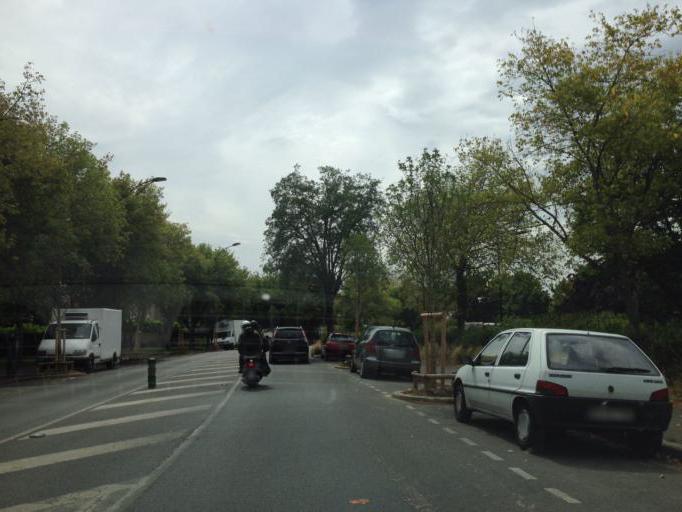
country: FR
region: Ile-de-France
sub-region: Departement des Hauts-de-Seine
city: Malakoff
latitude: 48.8237
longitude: 2.3001
